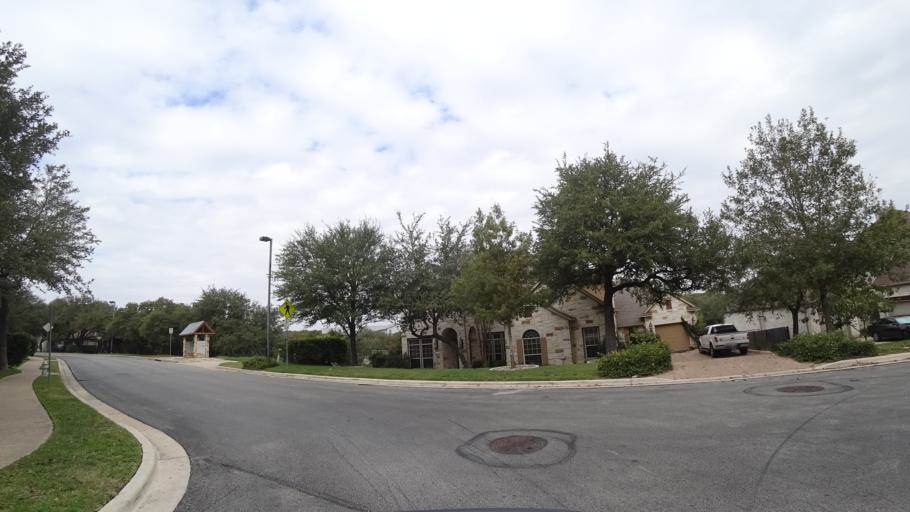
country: US
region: Texas
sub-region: Travis County
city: Shady Hollow
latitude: 30.1926
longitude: -97.9057
